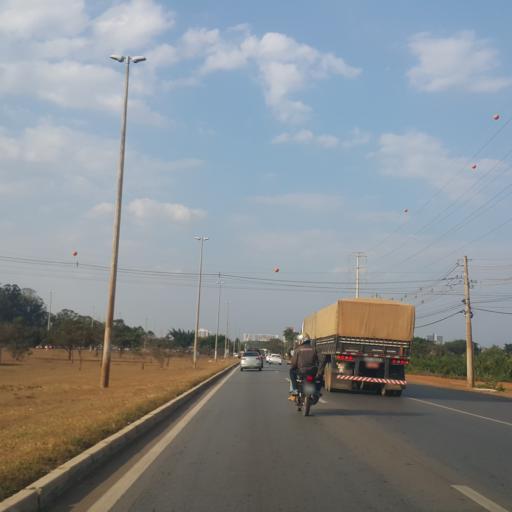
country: BR
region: Federal District
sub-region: Brasilia
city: Brasilia
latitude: -15.8787
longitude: -48.0518
